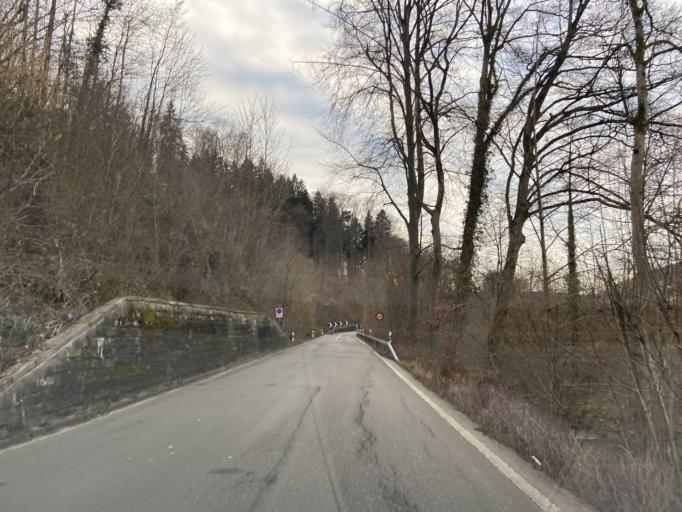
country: CH
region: Zurich
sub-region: Bezirk Winterthur
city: Stadt Winterthur (Kreis 1) / Bruehlberg
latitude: 47.5026
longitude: 8.7100
